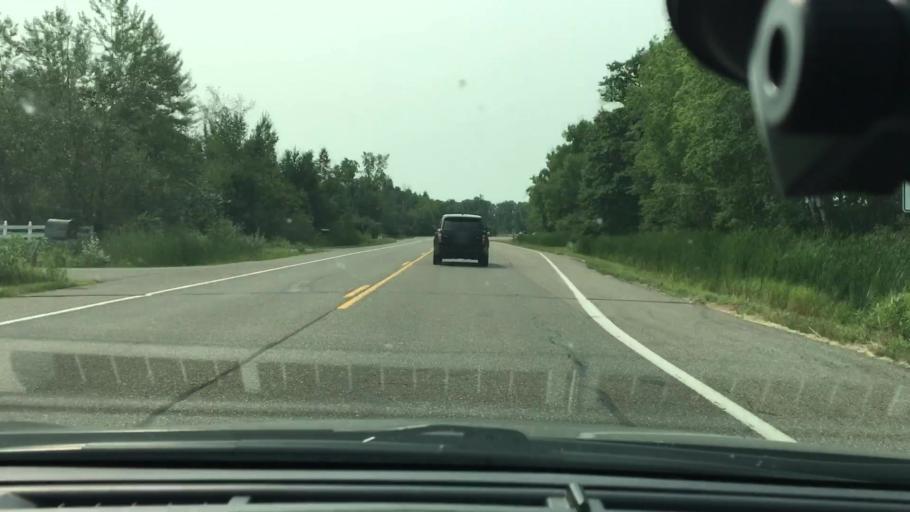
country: US
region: Minnesota
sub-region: Crow Wing County
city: Brainerd
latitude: 46.3879
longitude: -94.2232
